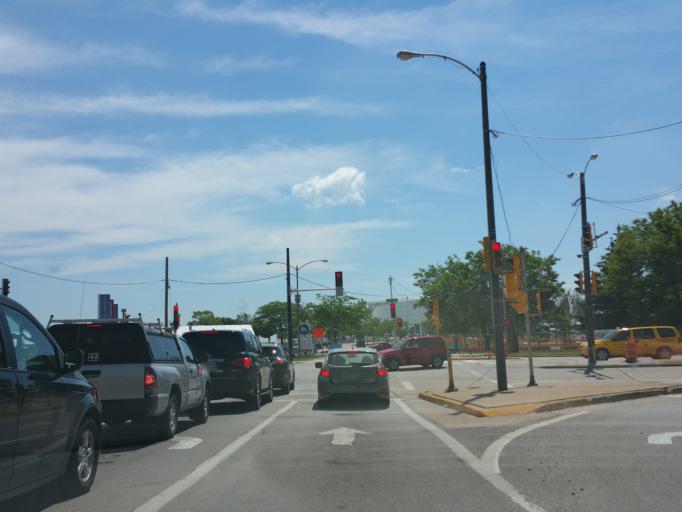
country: US
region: Wisconsin
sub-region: Milwaukee County
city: Milwaukee
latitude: 43.0376
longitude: -87.8994
